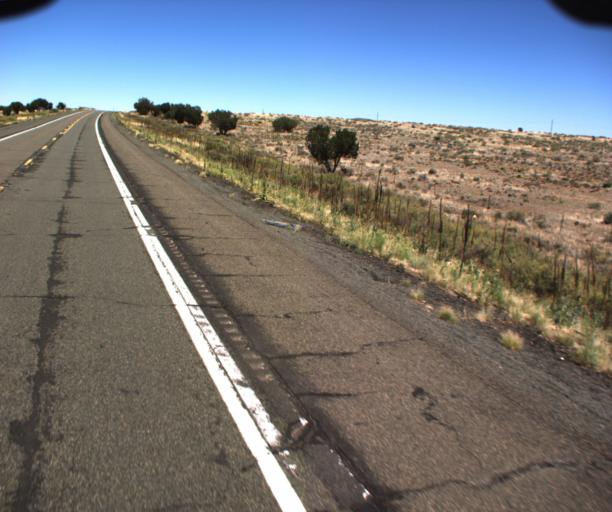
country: US
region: Arizona
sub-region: Coconino County
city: LeChee
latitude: 34.7748
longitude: -111.0052
